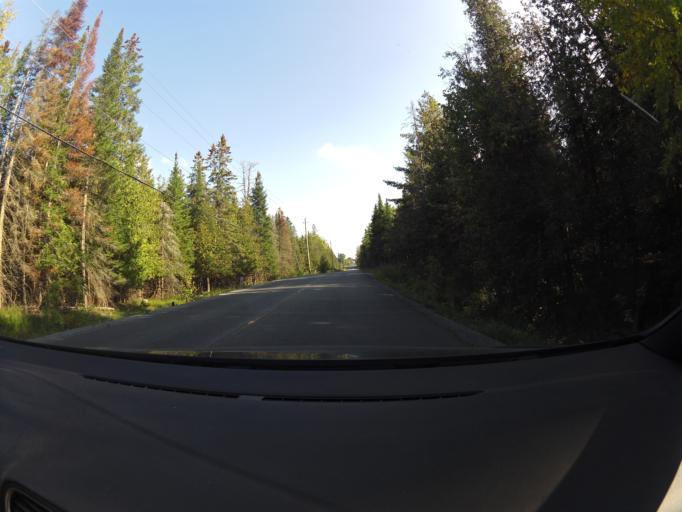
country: CA
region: Ontario
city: Arnprior
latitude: 45.4354
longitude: -76.2454
